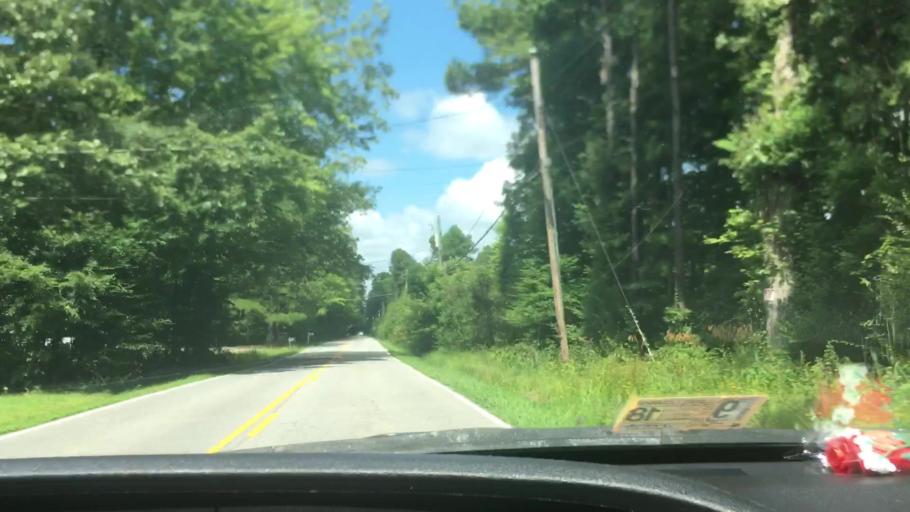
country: US
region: Virginia
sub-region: City of Virginia Beach
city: Virginia Beach
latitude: 36.7368
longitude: -76.1018
